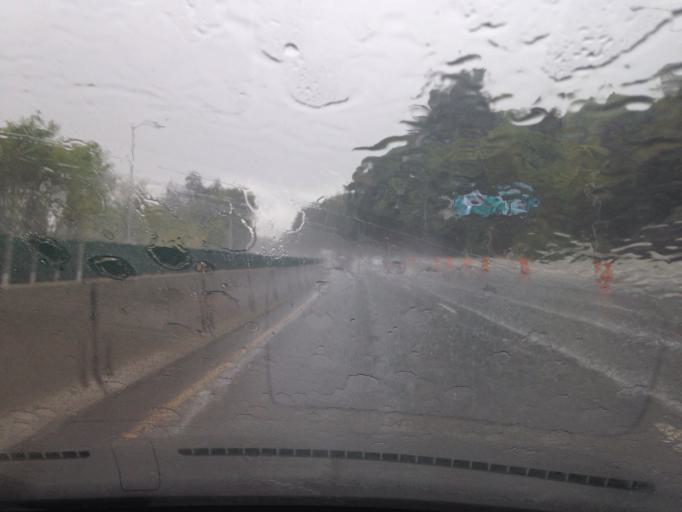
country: US
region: Oregon
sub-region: Multnomah County
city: Portland
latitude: 45.4771
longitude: -122.6788
